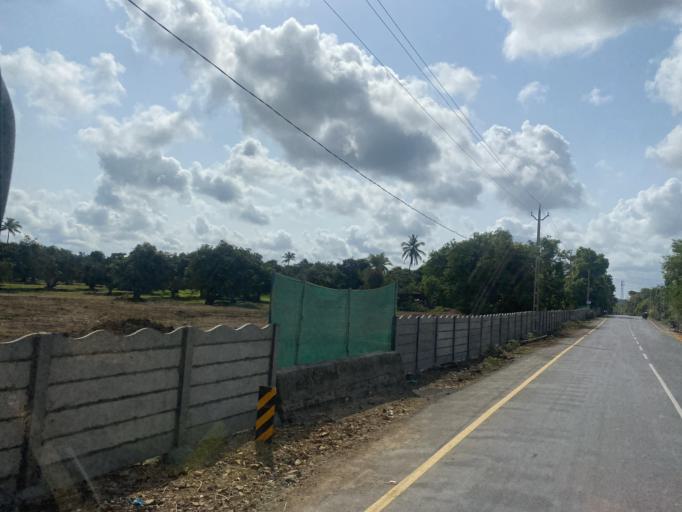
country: IN
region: Daman and Diu
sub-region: Daman District
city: Daman
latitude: 20.3297
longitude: 72.8133
